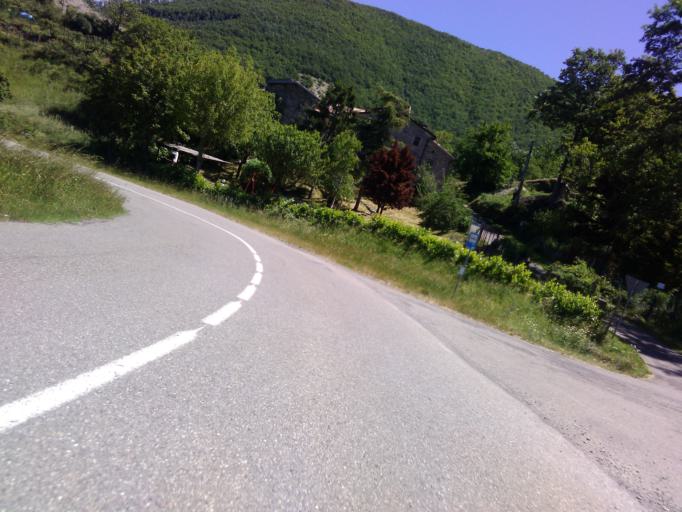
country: IT
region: Emilia-Romagna
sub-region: Provincia di Parma
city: Terenzo
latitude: 44.5654
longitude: 10.0510
